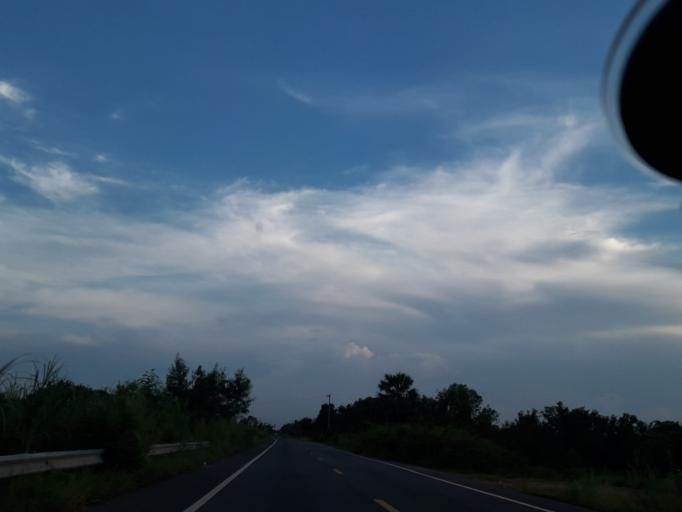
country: TH
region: Sara Buri
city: Nong Khae
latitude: 14.2946
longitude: 100.8911
